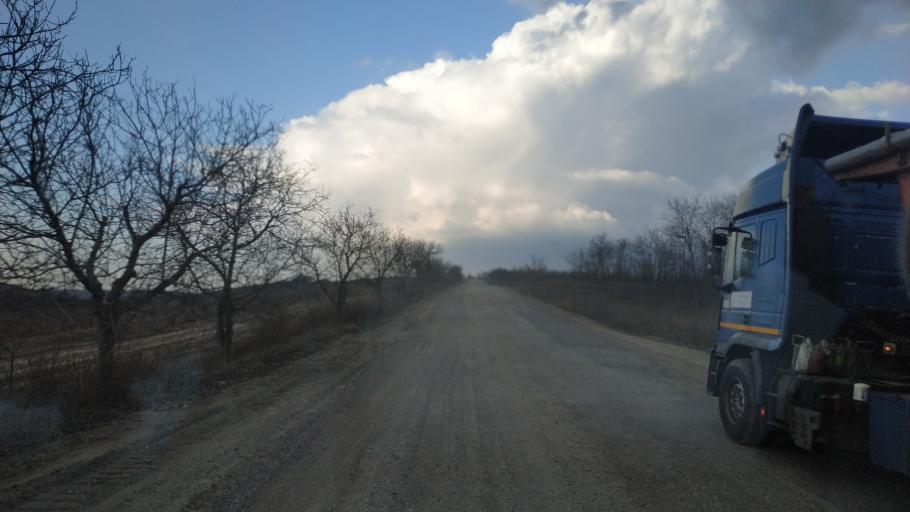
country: MD
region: Anenii Noi
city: Anenii Noi
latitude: 46.9862
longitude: 29.2843
